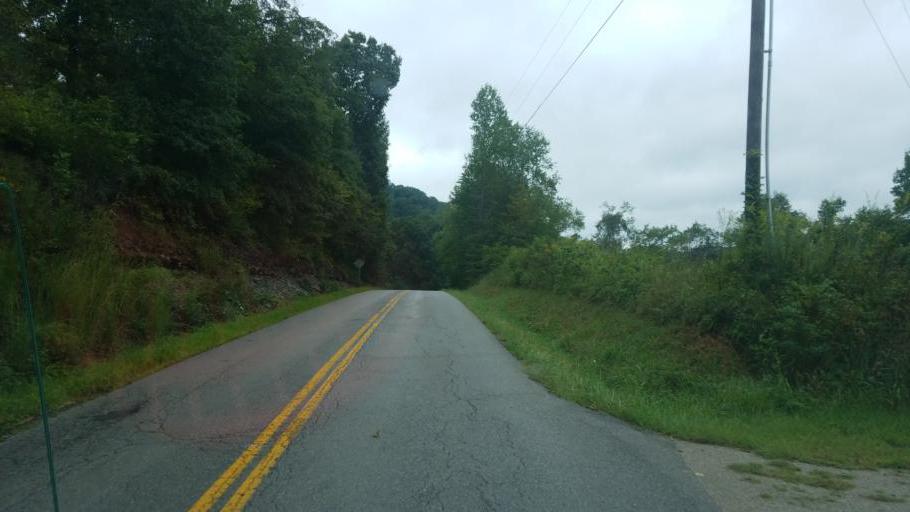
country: US
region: Kentucky
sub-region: Fleming County
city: Flemingsburg
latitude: 38.3826
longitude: -83.5422
